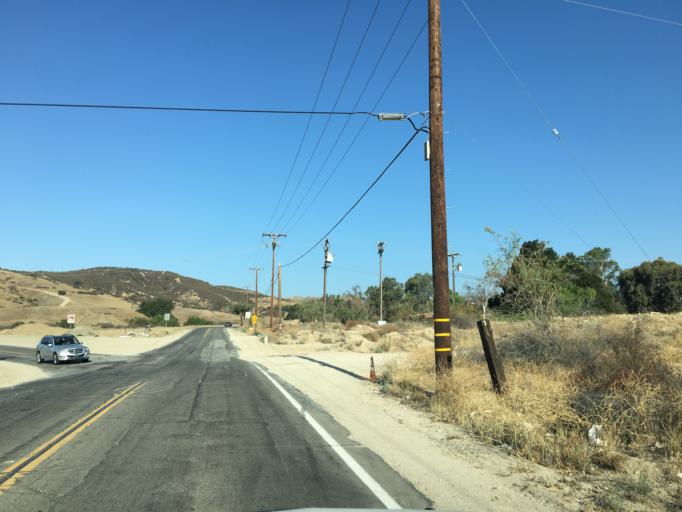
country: US
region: California
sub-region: Los Angeles County
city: Val Verde
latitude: 34.4572
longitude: -118.6406
